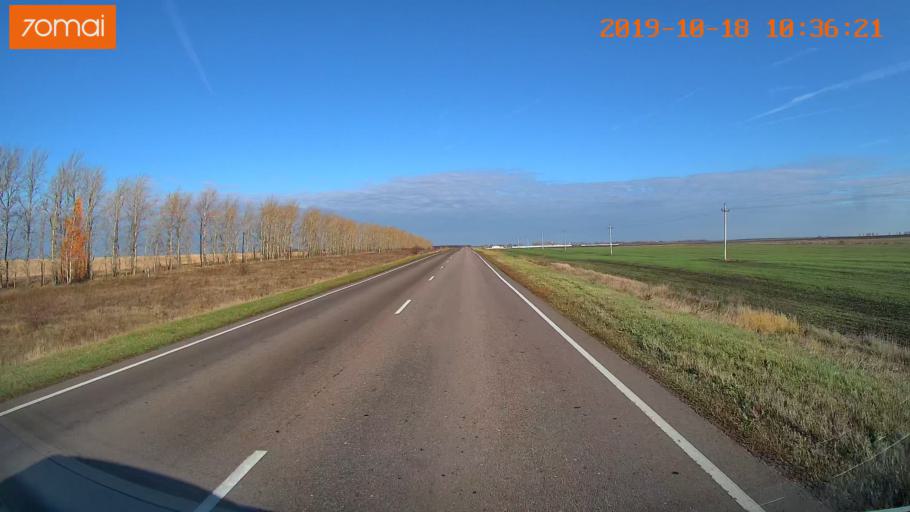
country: RU
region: Tula
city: Kurkino
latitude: 53.5471
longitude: 38.6249
